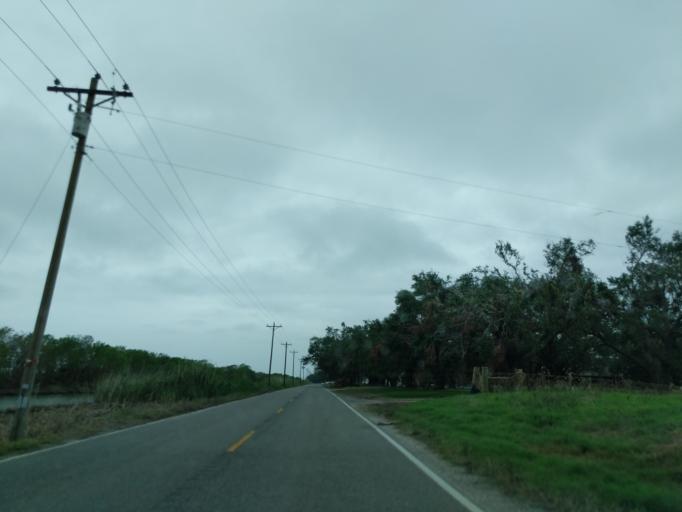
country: US
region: Louisiana
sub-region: Jefferson Davis Parish
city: Lake Arthur
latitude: 29.7506
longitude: -92.9034
